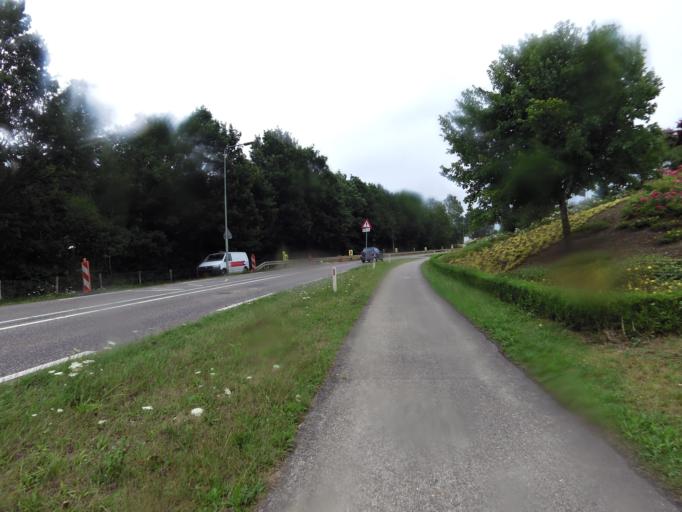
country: NL
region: Limburg
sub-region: Gemeente Kerkrade
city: Kerkrade
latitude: 50.8912
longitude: 6.0404
